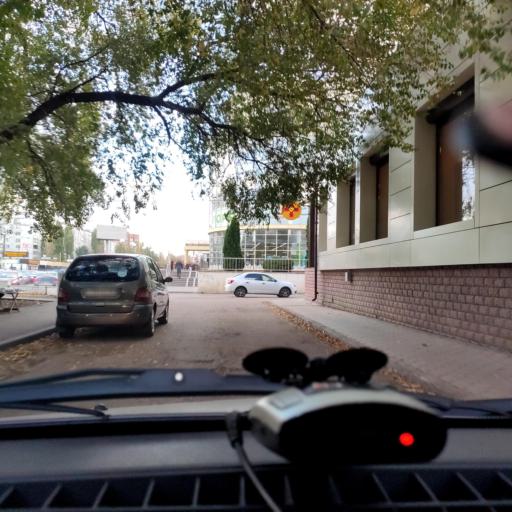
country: RU
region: Voronezj
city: Podgornoye
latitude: 51.7060
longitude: 39.1508
